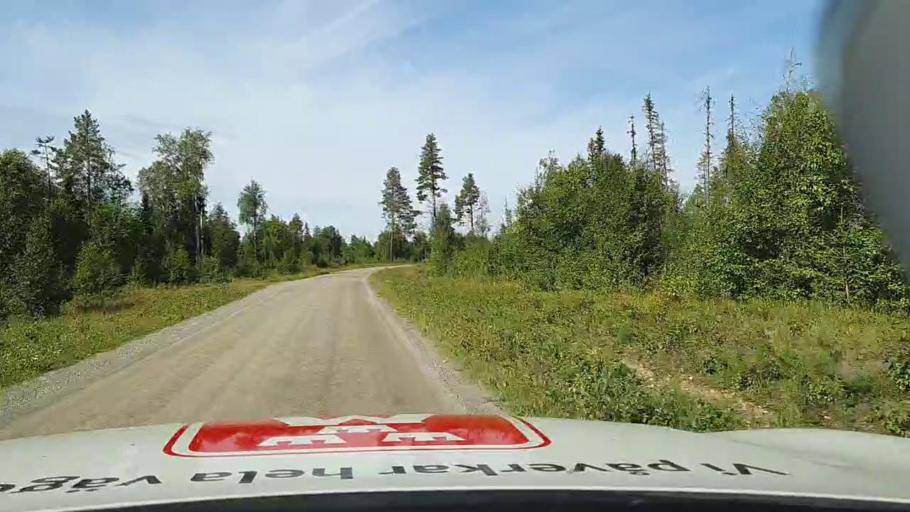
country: SE
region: Jaemtland
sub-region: Stroemsunds Kommun
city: Stroemsund
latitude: 63.7119
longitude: 15.3046
